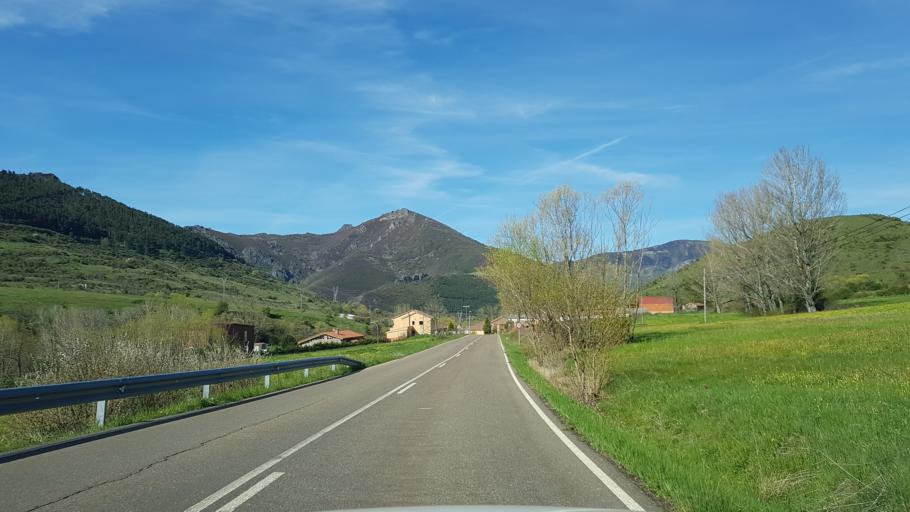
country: ES
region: Castille and Leon
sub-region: Provincia de Leon
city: Villamanin
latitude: 42.9439
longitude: -5.6415
